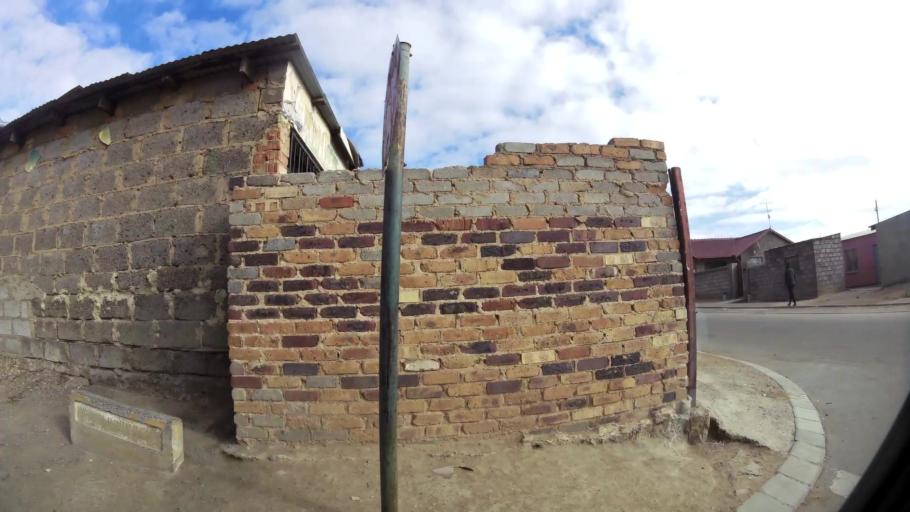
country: ZA
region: Gauteng
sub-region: City of Johannesburg Metropolitan Municipality
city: Modderfontein
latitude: -26.0429
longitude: 28.1853
